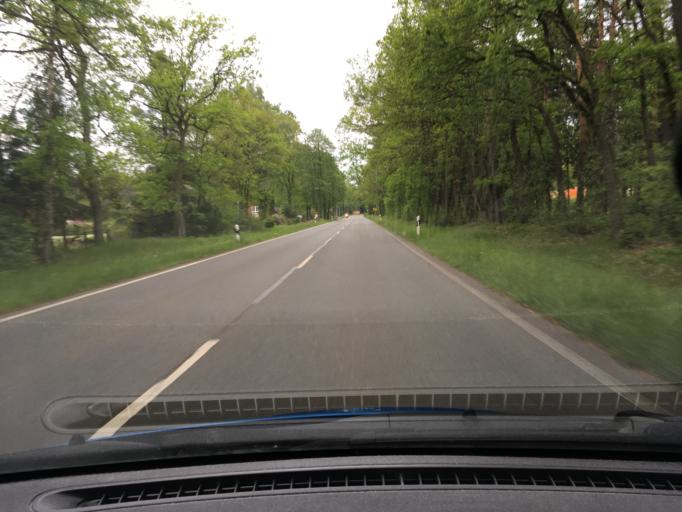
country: DE
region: Lower Saxony
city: Bispingen
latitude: 53.0940
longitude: 10.0336
